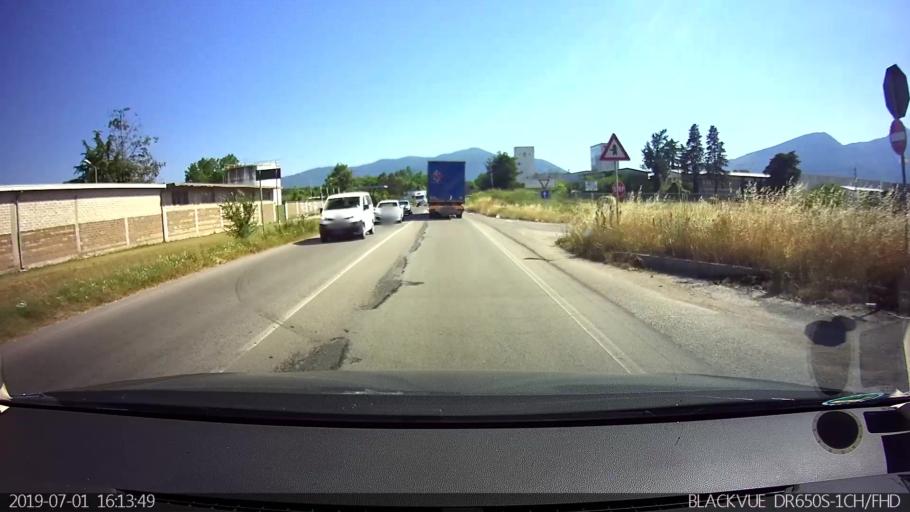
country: IT
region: Latium
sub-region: Provincia di Frosinone
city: Ceccano
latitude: 41.6046
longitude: 13.3006
